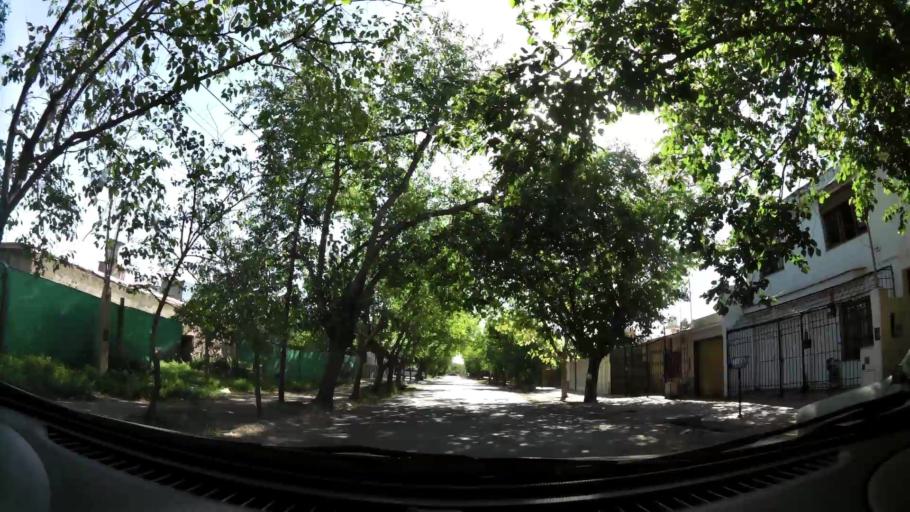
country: AR
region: Mendoza
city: Mendoza
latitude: -32.9041
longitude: -68.8158
